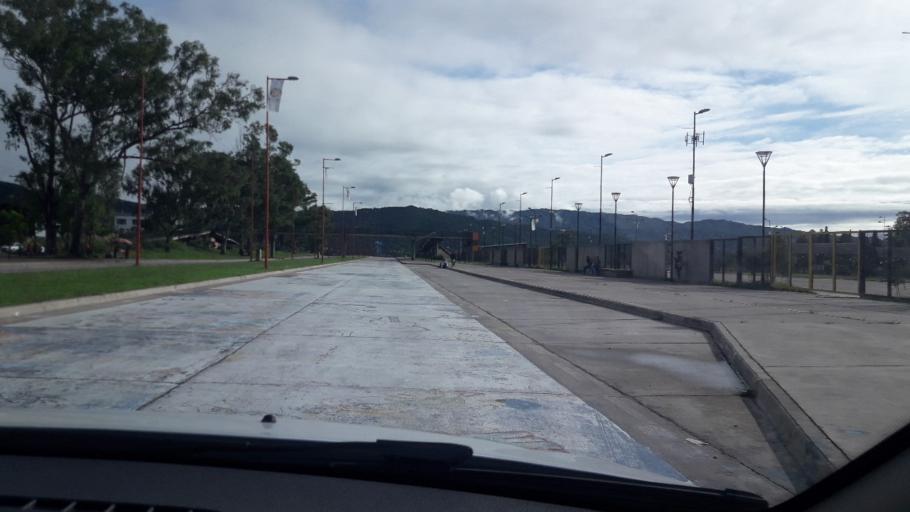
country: AR
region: Jujuy
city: San Salvador de Jujuy
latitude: -24.1830
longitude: -65.3315
